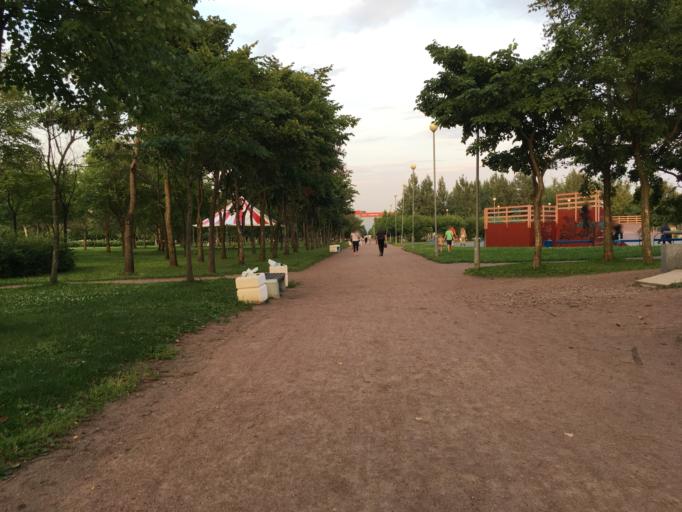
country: RU
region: Leningrad
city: Untolovo
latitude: 59.9836
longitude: 30.1966
